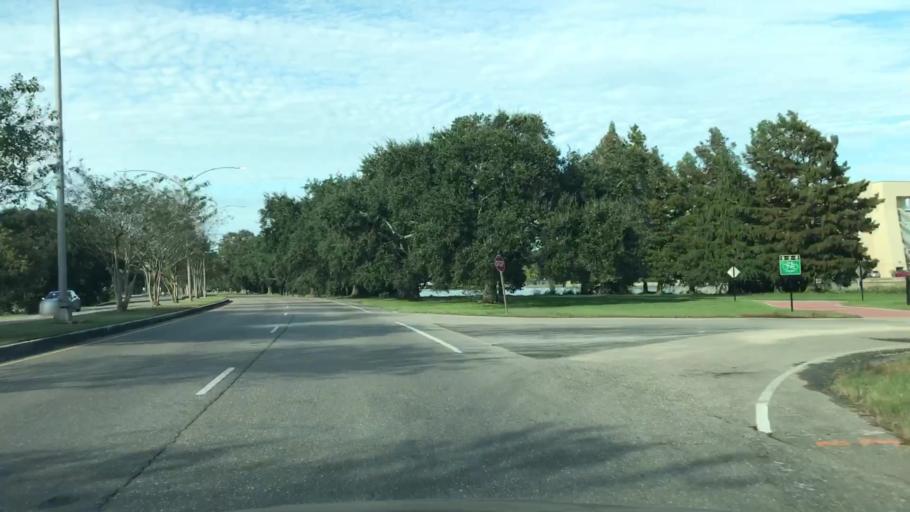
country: US
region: Louisiana
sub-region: Orleans Parish
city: New Orleans
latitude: 29.9964
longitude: -90.0859
